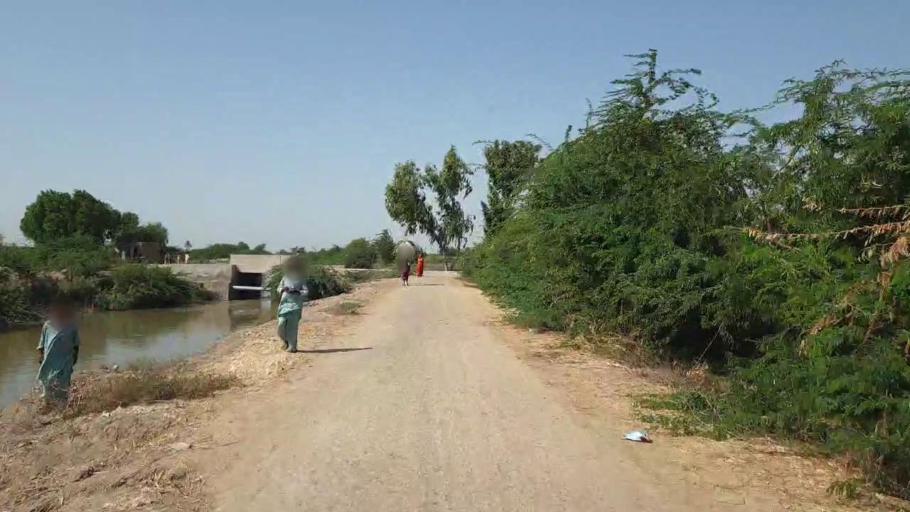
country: PK
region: Sindh
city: Tando Bago
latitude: 24.7429
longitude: 69.0653
